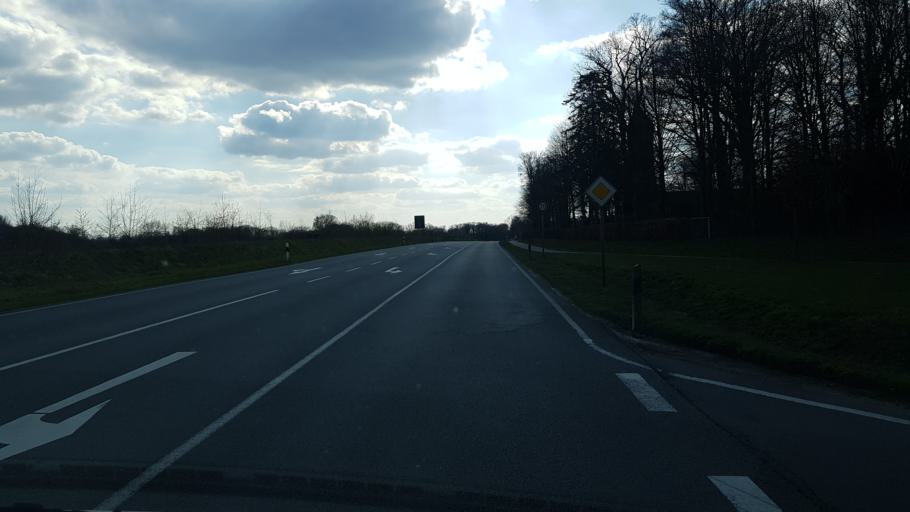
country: DE
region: Lower Saxony
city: Rastede
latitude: 53.2300
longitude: 8.2664
